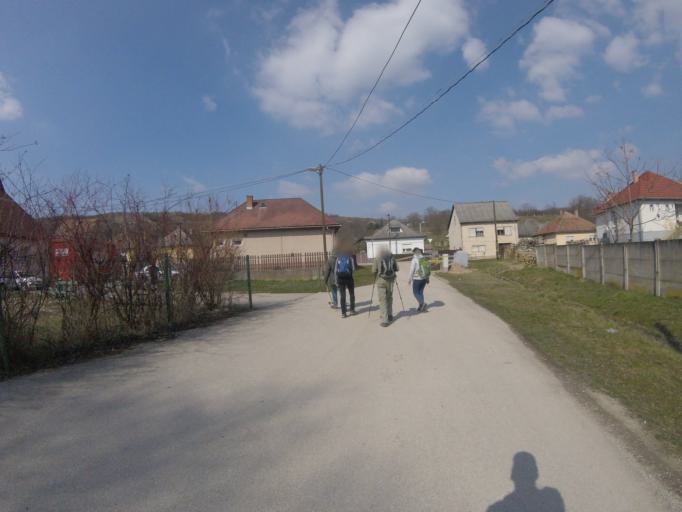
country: HU
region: Komarom-Esztergom
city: Nyergesujfalu
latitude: 47.7567
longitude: 18.5554
